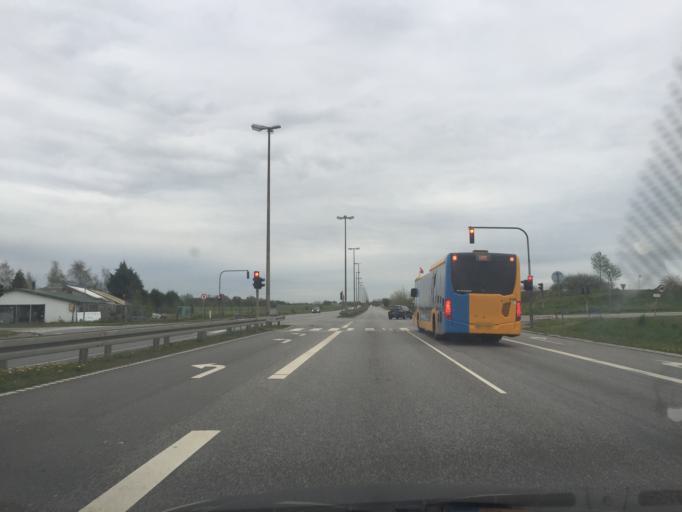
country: DK
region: Capital Region
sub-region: Hoje-Taastrup Kommune
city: Taastrup
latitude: 55.6280
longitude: 12.3051
